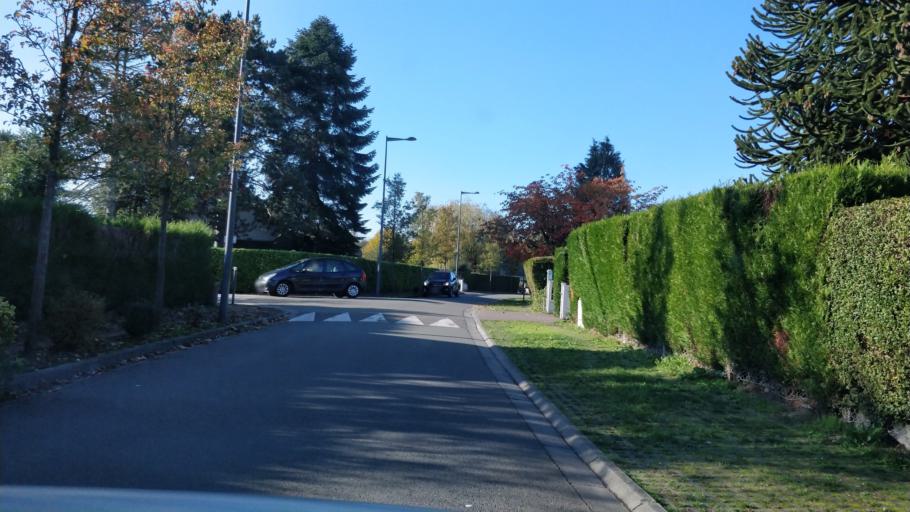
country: FR
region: Haute-Normandie
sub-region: Departement de la Seine-Maritime
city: Bois-Guillaume
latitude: 49.4685
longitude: 1.1379
